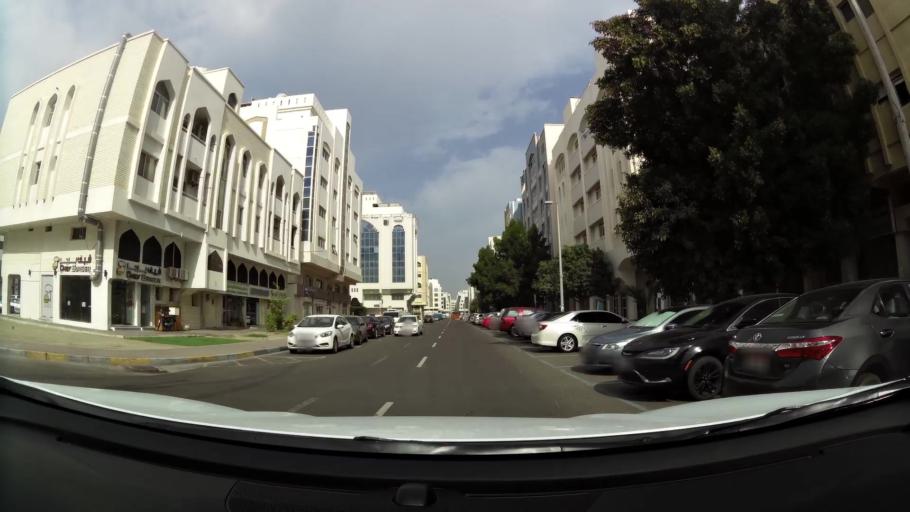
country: AE
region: Abu Dhabi
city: Abu Dhabi
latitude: 24.4611
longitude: 54.3853
